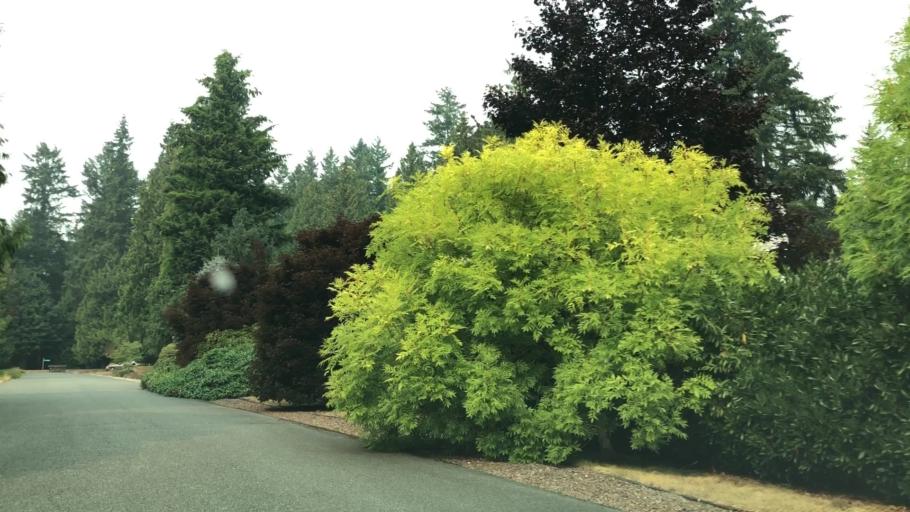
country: US
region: Washington
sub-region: King County
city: Cottage Lake
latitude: 47.7587
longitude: -122.0854
